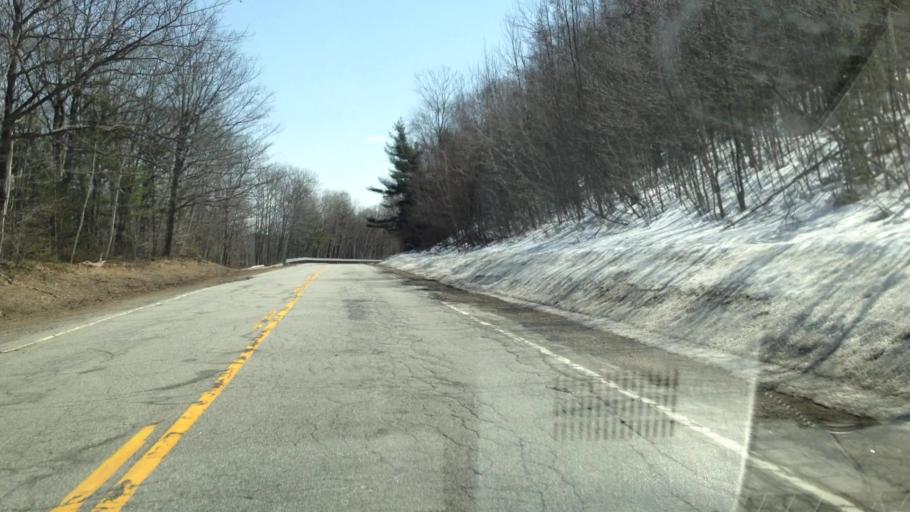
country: US
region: New Hampshire
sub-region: Sullivan County
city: Springfield
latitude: 43.4906
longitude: -71.9835
